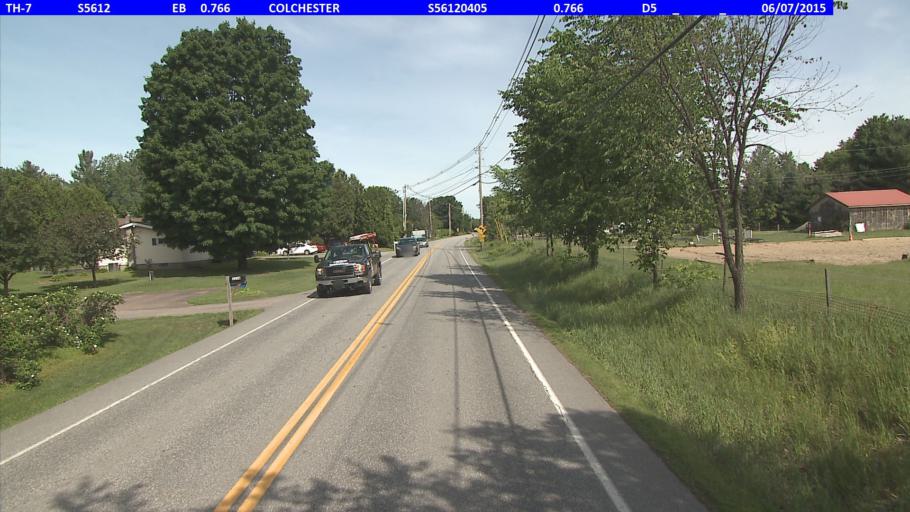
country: US
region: Vermont
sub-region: Chittenden County
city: Colchester
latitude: 44.5207
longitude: -73.1508
